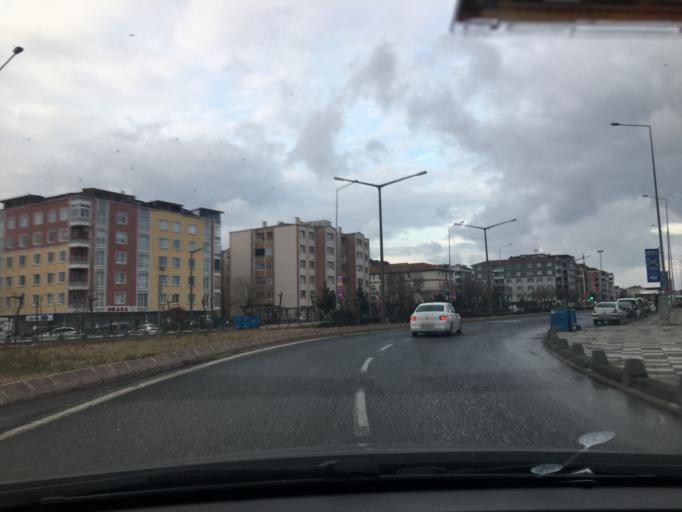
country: TR
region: Tekirdag
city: Cerkezkoey
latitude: 41.2806
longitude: 27.9820
